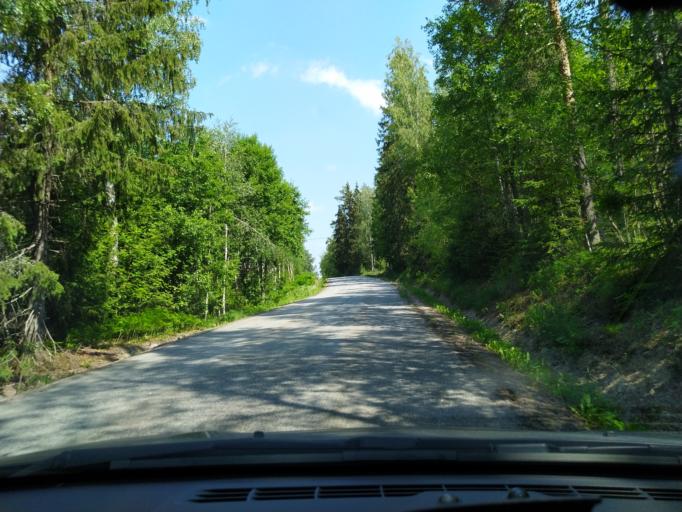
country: FI
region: Uusimaa
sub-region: Helsinki
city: Saukkola
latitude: 60.3626
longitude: 24.0993
